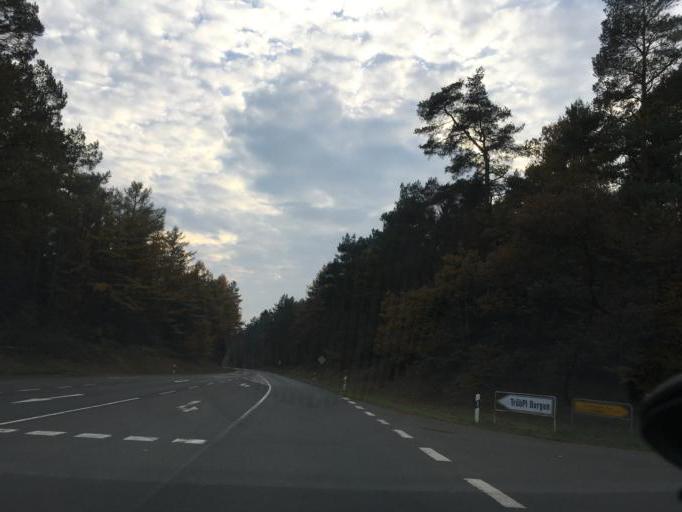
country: DE
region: Lower Saxony
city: Wietzendorf
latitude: 52.9972
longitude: 9.9976
